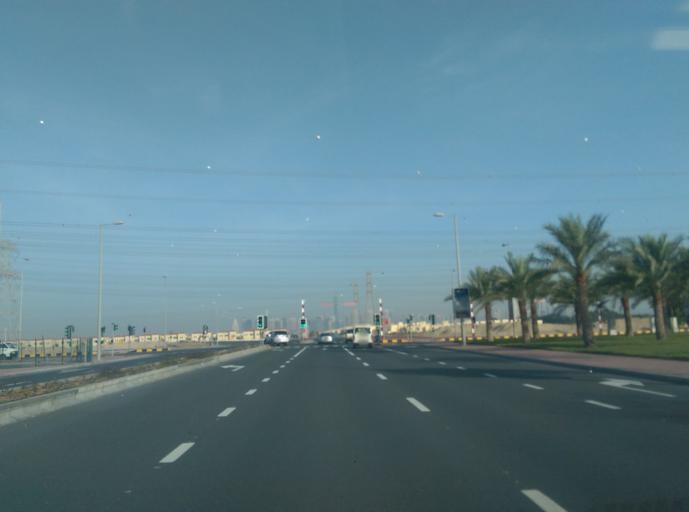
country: AE
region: Dubai
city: Dubai
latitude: 25.0371
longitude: 55.1755
